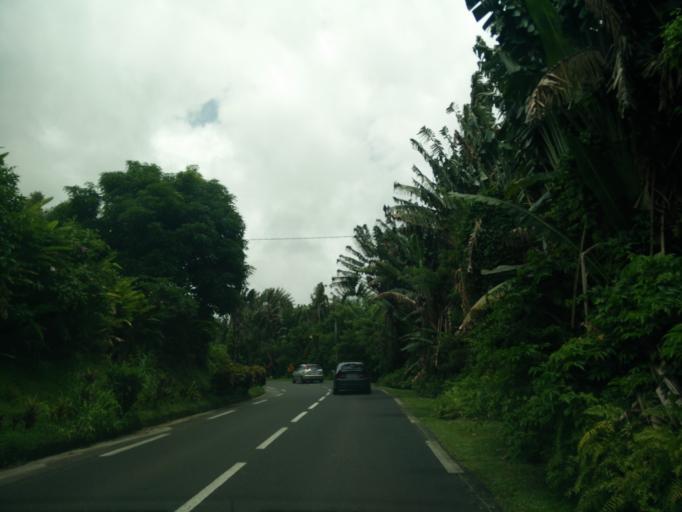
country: MQ
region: Martinique
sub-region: Martinique
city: Le Morne-Rouge
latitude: 14.7622
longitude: -61.1545
